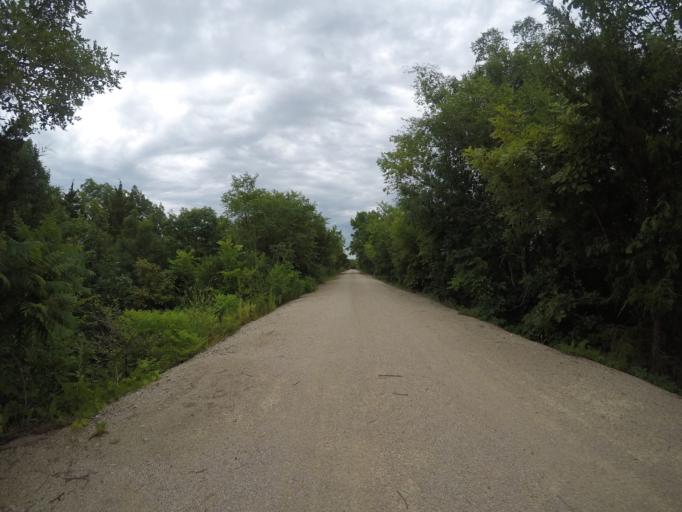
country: US
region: Kansas
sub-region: Anderson County
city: Garnett
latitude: 38.3083
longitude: -95.2471
